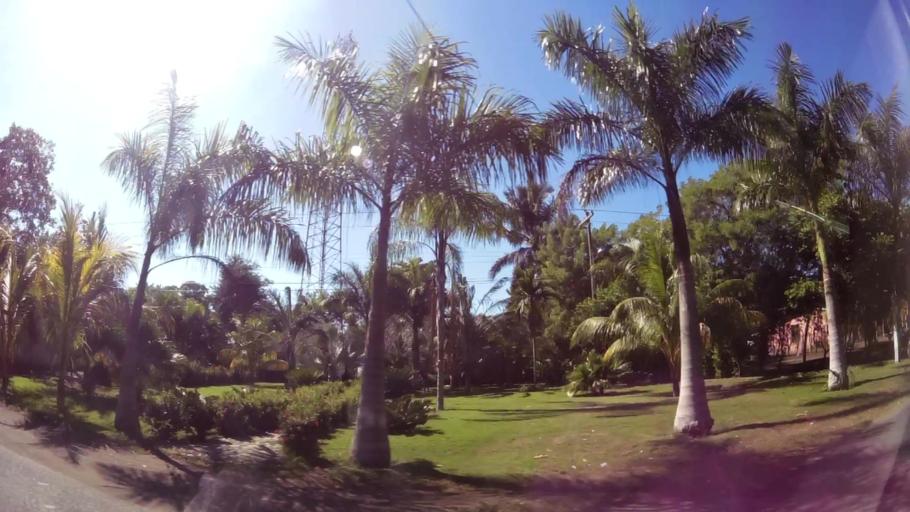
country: GT
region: Santa Rosa
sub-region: Municipio de Taxisco
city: Taxisco
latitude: 13.9115
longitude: -90.5308
